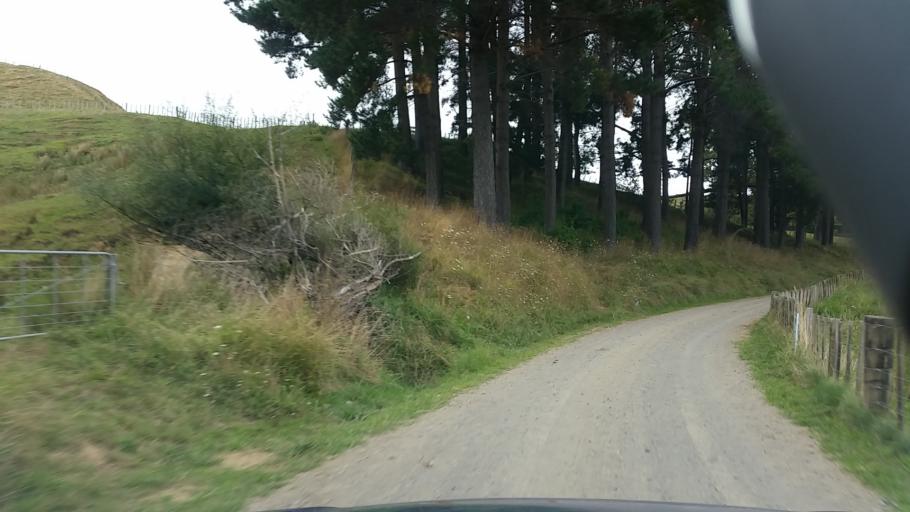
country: NZ
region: Taranaki
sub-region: South Taranaki District
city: Eltham
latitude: -39.3182
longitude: 174.5327
